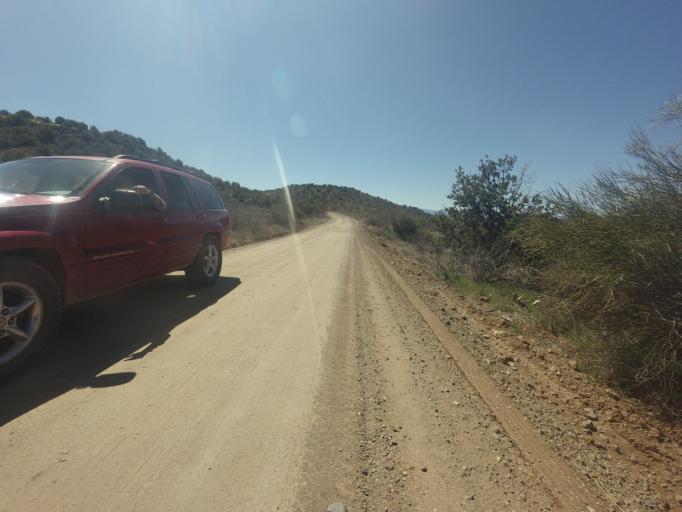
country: US
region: Arizona
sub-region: Yavapai County
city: Lake Montezuma
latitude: 34.6652
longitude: -111.7140
